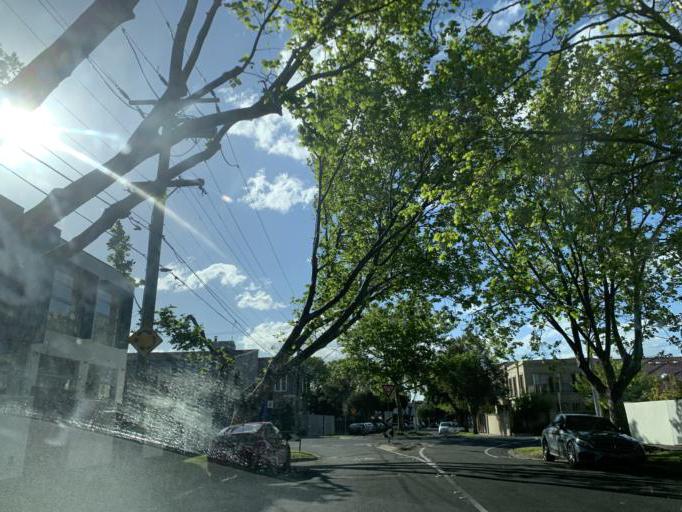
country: AU
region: Victoria
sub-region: Bayside
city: North Brighton
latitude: -37.9113
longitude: 144.9951
